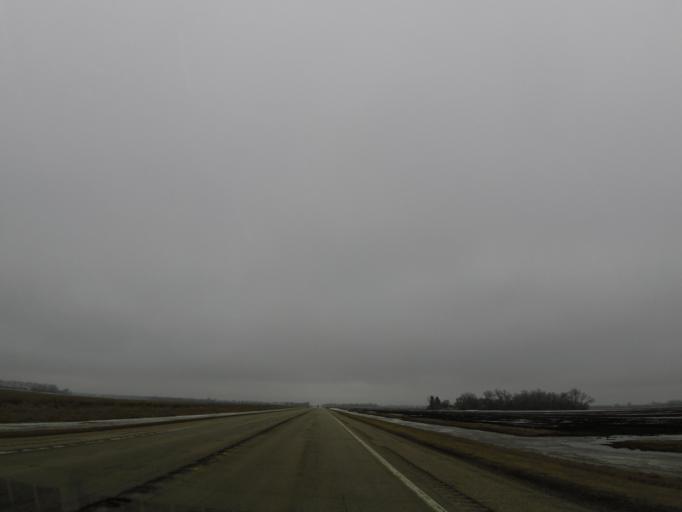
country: US
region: North Dakota
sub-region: Walsh County
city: Grafton
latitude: 48.5644
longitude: -97.4480
